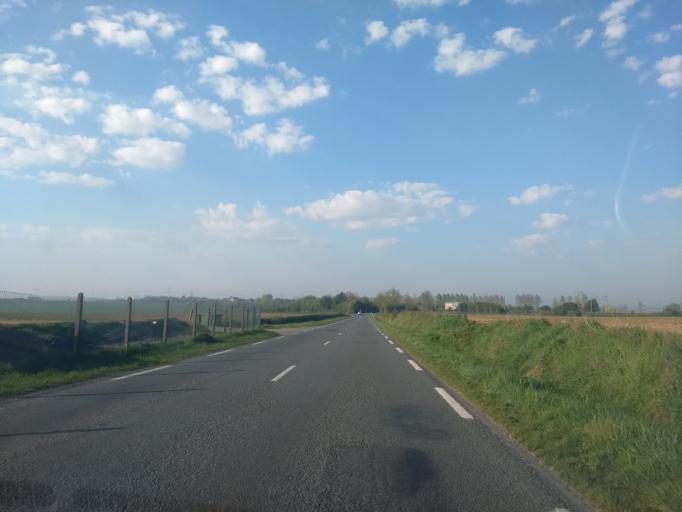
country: FR
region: Nord-Pas-de-Calais
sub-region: Departement du Pas-de-Calais
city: Agny
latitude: 50.2465
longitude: 2.7687
